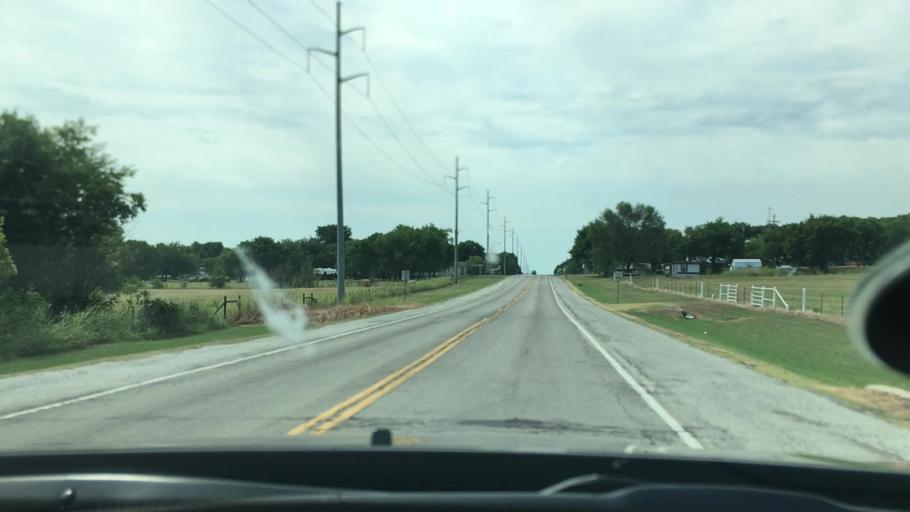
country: US
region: Oklahoma
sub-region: Carter County
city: Ardmore
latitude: 34.3180
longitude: -97.1430
